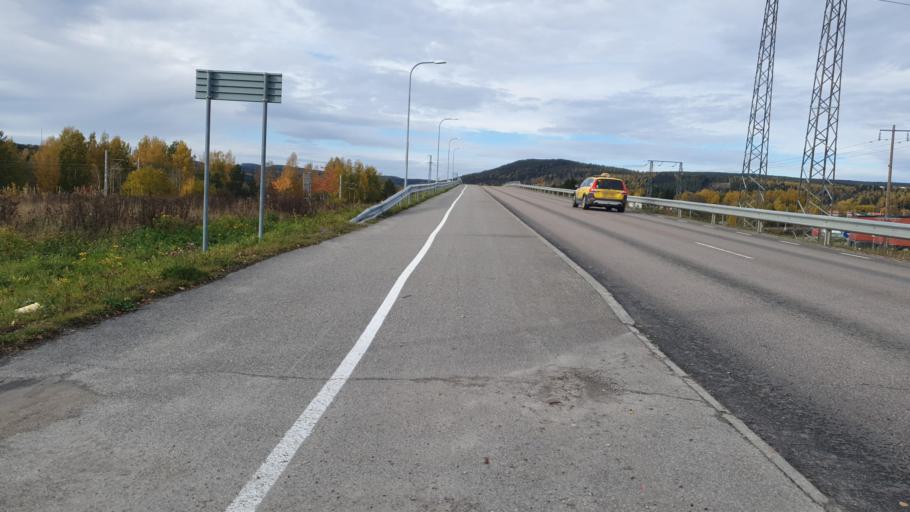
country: SE
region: Vaesternorrland
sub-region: Sundsvalls Kommun
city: Sundsvall
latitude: 62.4061
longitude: 17.2366
